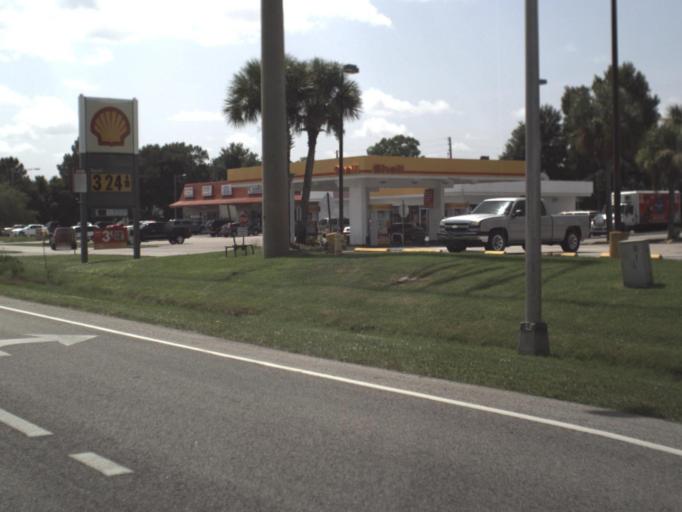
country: US
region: Florida
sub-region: Highlands County
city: Avon Park
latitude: 27.5389
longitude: -81.5040
